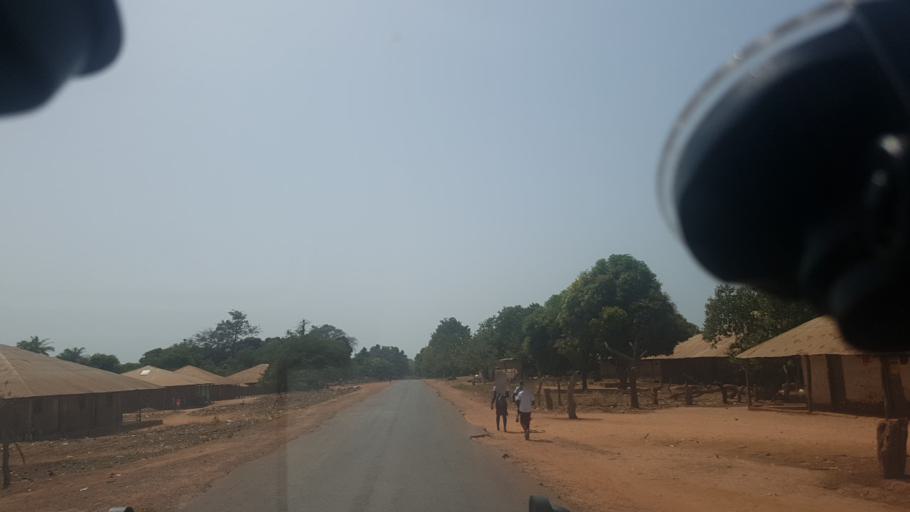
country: GW
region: Cacheu
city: Cacheu
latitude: 12.4092
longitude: -16.0470
